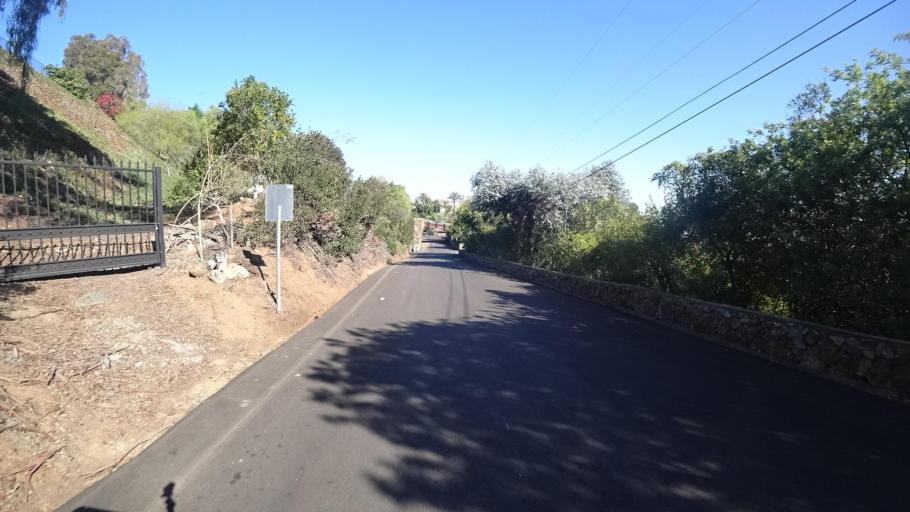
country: US
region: California
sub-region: San Diego County
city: Casa de Oro-Mount Helix
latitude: 32.7678
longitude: -116.9812
